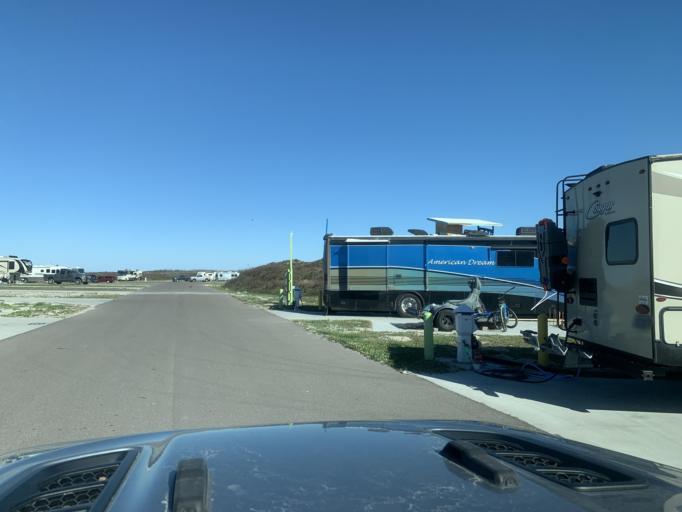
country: US
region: Texas
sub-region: Nueces County
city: Port Aransas
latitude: 27.8318
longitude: -97.0508
